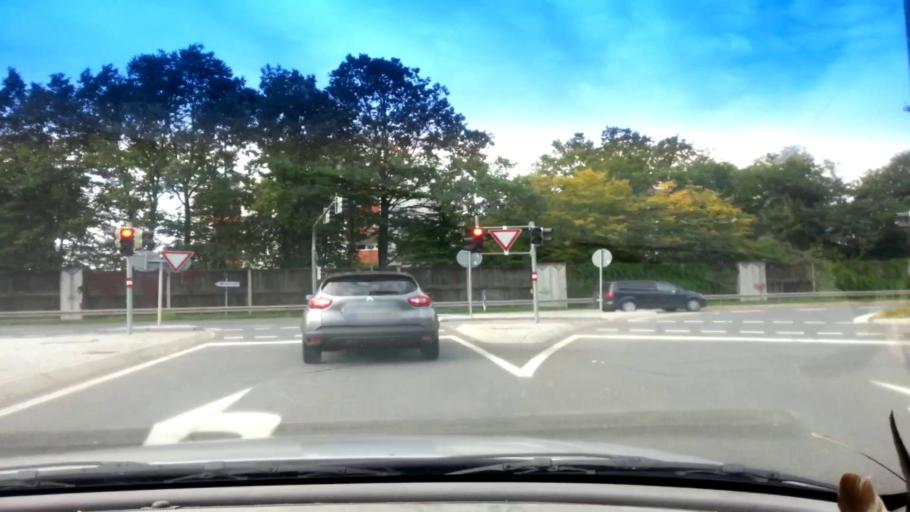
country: DE
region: Bavaria
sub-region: Upper Franconia
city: Gundelsheim
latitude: 49.9214
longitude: 10.9310
